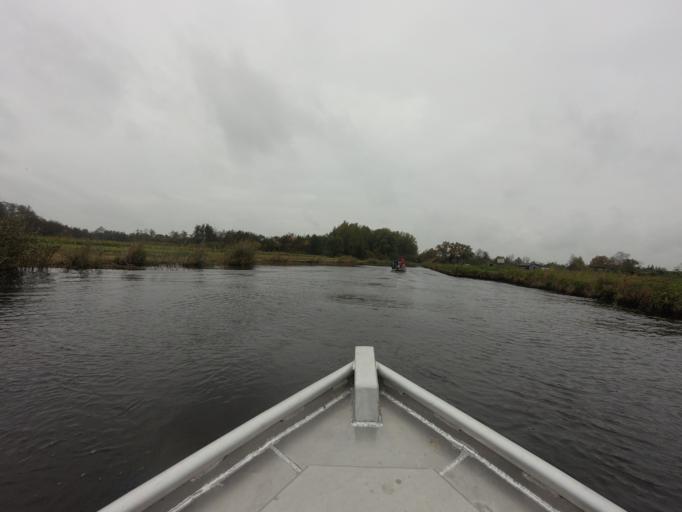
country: NL
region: Overijssel
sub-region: Gemeente Steenwijkerland
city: Blokzijl
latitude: 52.7734
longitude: 5.9683
